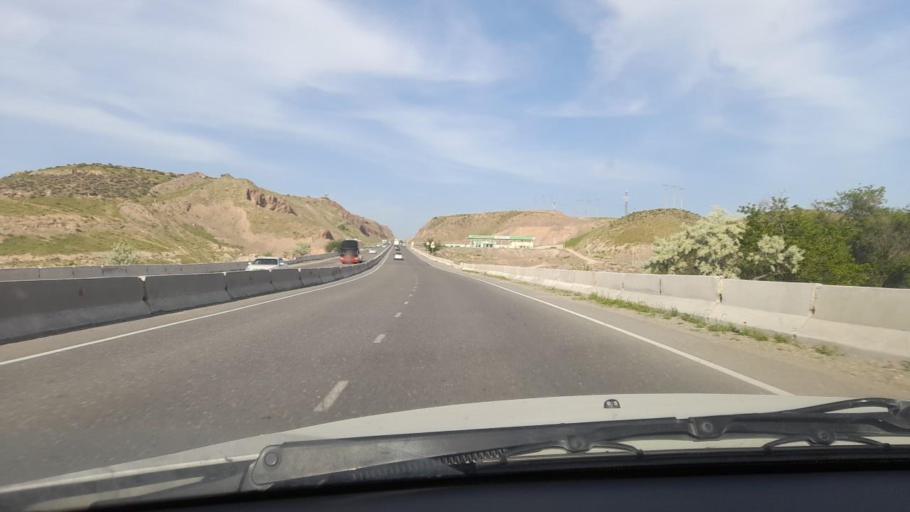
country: UZ
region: Jizzax
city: Jizzax
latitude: 40.0372
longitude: 67.6382
